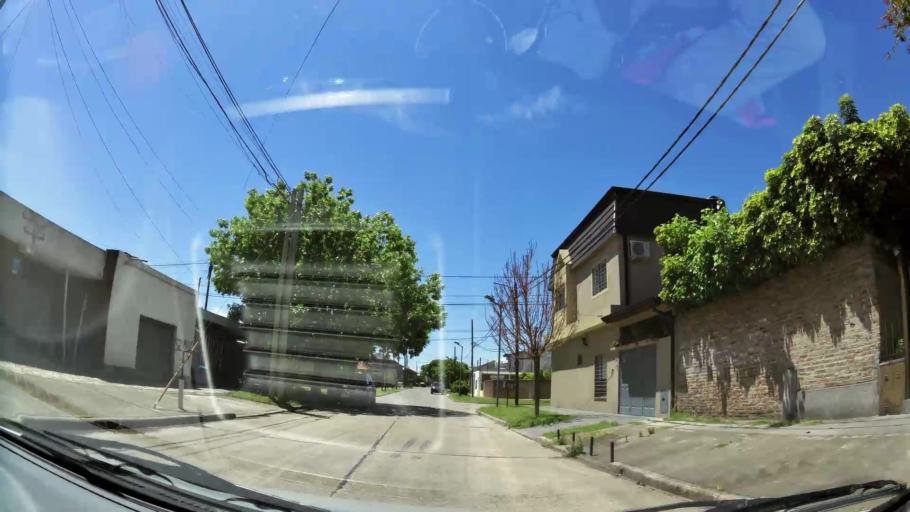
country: AR
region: Buenos Aires
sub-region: Partido de Quilmes
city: Quilmes
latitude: -34.7476
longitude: -58.2834
